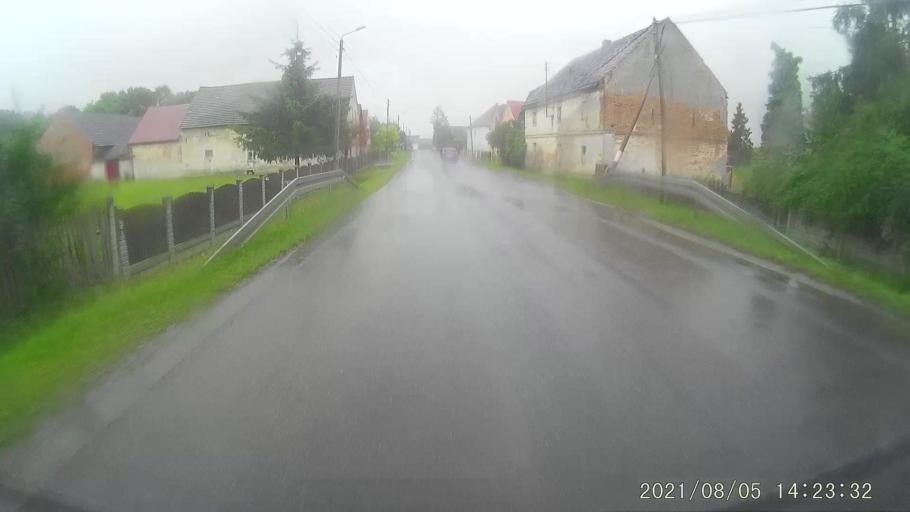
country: PL
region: Opole Voivodeship
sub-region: Powiat nyski
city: Korfantow
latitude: 50.4824
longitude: 17.6461
